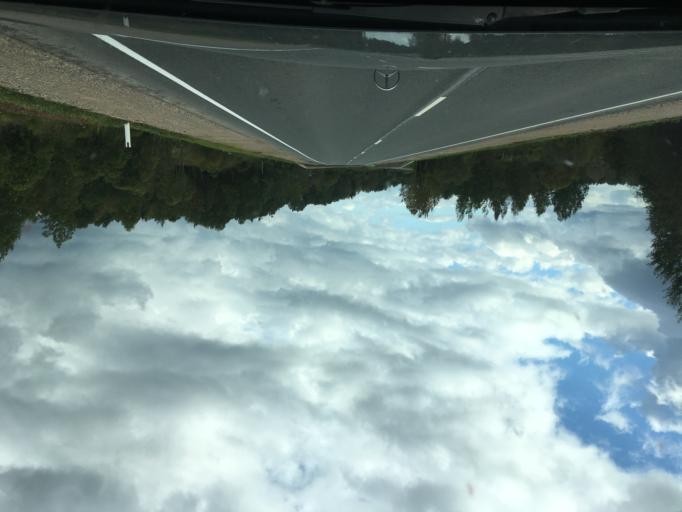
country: RU
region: Pskov
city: Velikiye Luki
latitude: 56.2975
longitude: 31.0430
